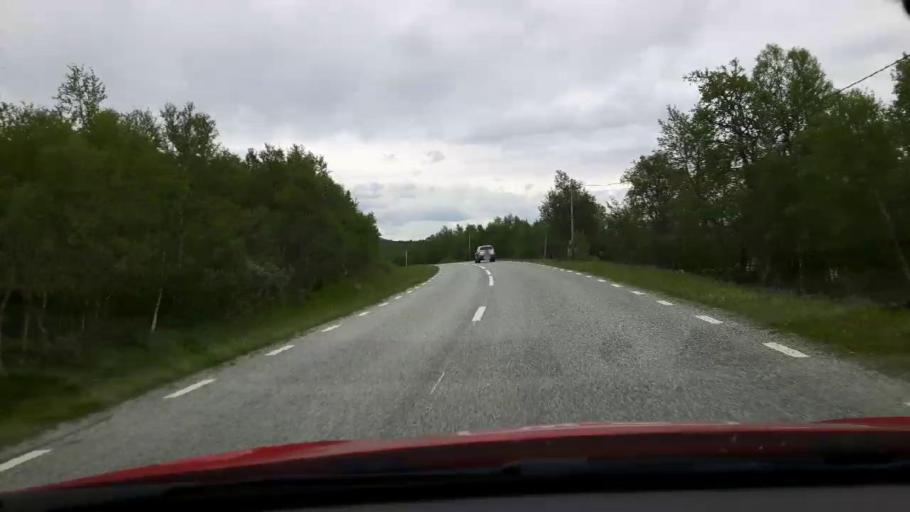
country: NO
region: Sor-Trondelag
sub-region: Tydal
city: Aas
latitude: 62.6020
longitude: 12.1710
